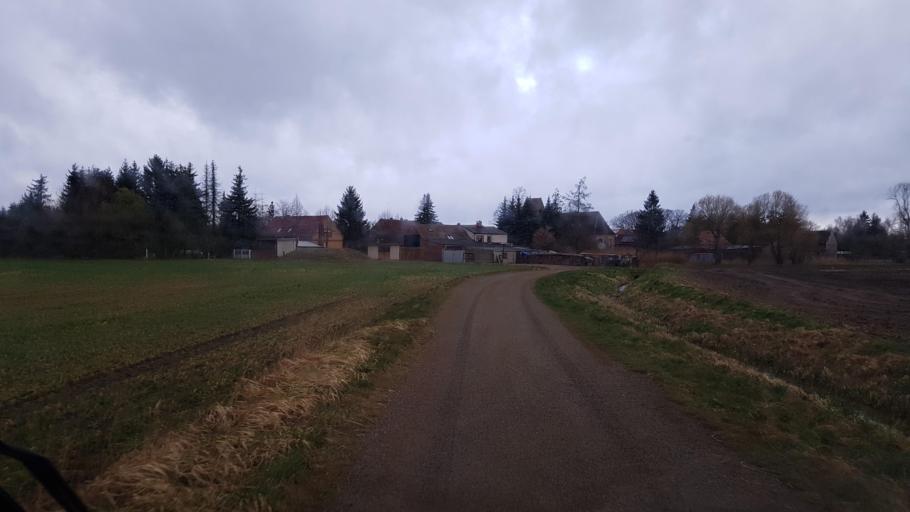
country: DE
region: Brandenburg
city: Bronkow
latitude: 51.6442
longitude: 13.9301
